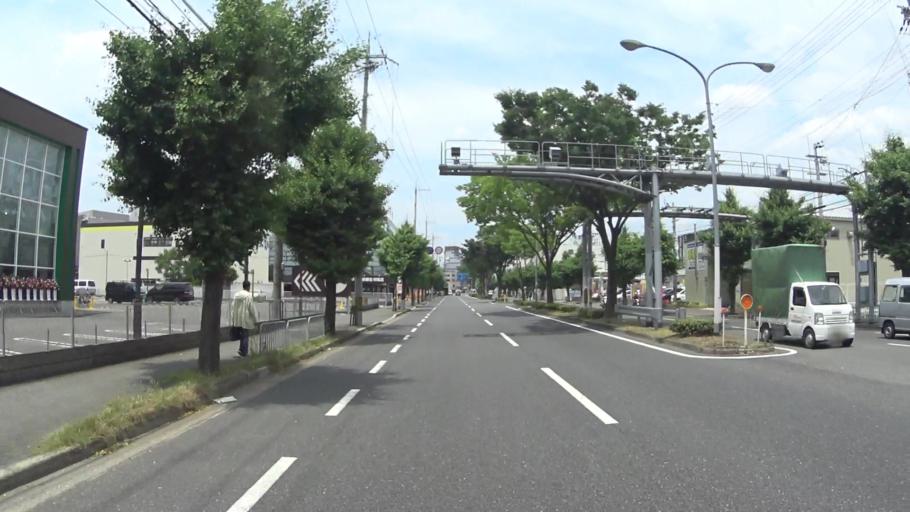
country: JP
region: Kyoto
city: Muko
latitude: 34.9817
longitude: 135.7217
